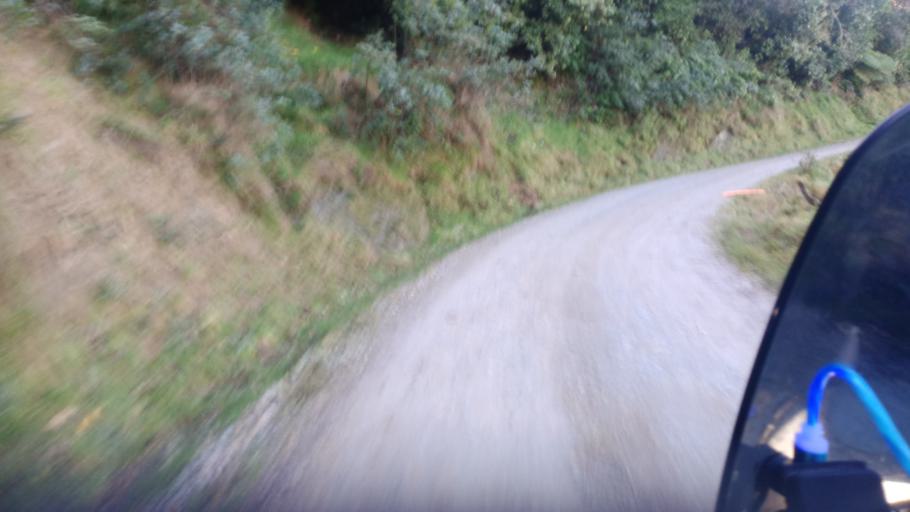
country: NZ
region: Hawke's Bay
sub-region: Wairoa District
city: Wairoa
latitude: -38.6655
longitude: 177.4790
